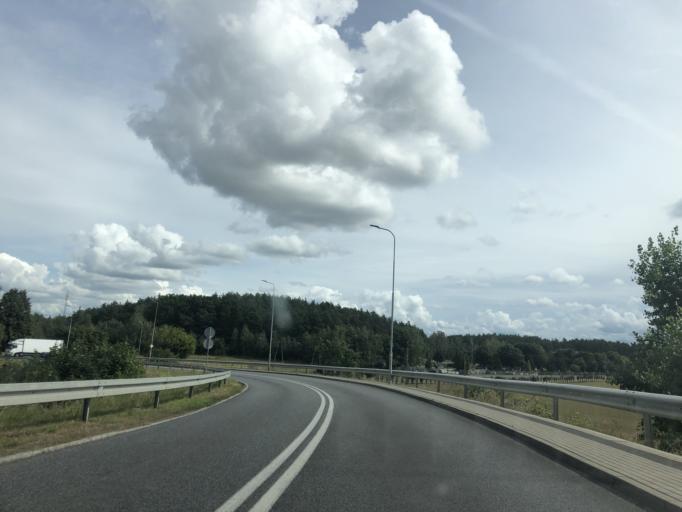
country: PL
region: Greater Poland Voivodeship
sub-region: Powiat czarnkowsko-trzcianecki
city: Trzcianka
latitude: 53.0432
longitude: 16.4784
